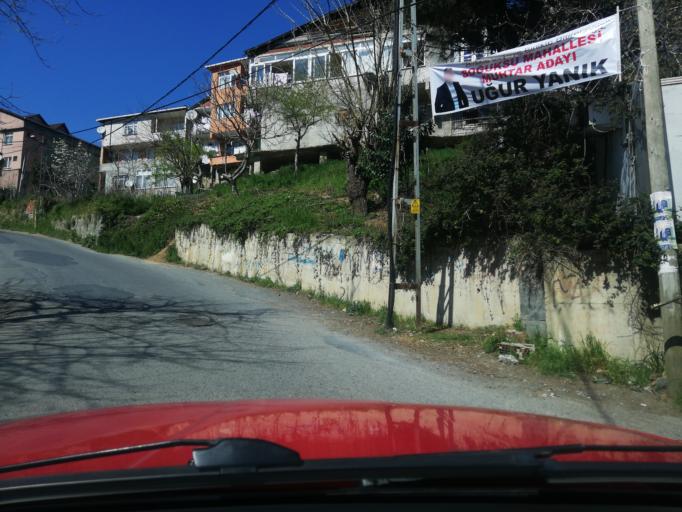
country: TR
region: Istanbul
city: Mahmut Sevket Pasa
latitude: 41.1132
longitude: 29.1126
